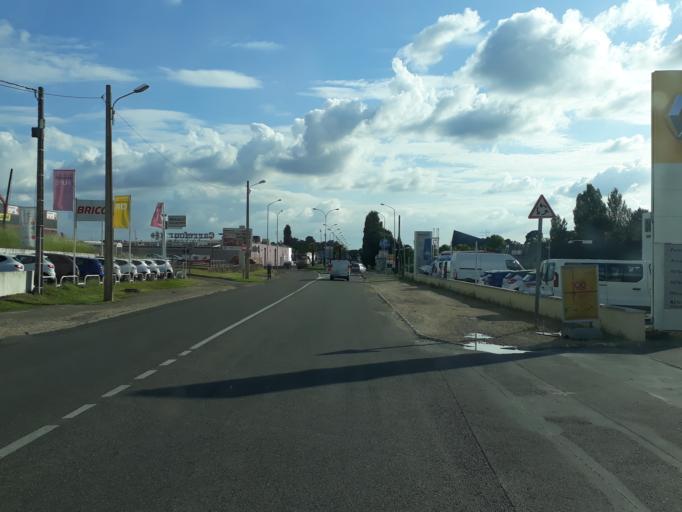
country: FR
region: Aquitaine
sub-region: Departement des Landes
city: Mont-de-Marsan
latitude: 43.9032
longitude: -0.4786
